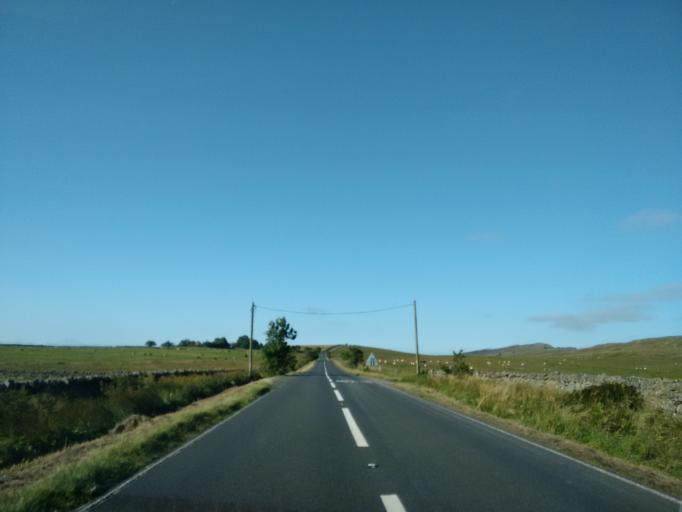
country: GB
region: England
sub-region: Northumberland
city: Bardon Mill
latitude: 55.0025
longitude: -2.3539
